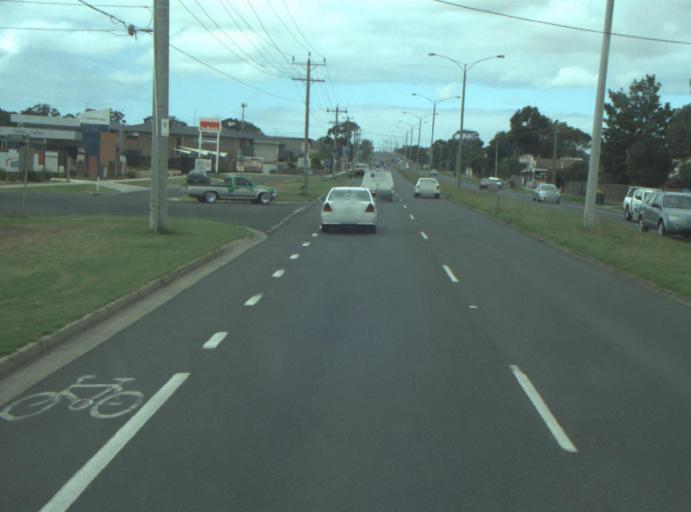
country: AU
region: Victoria
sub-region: Greater Geelong
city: Breakwater
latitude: -38.1979
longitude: 144.3420
